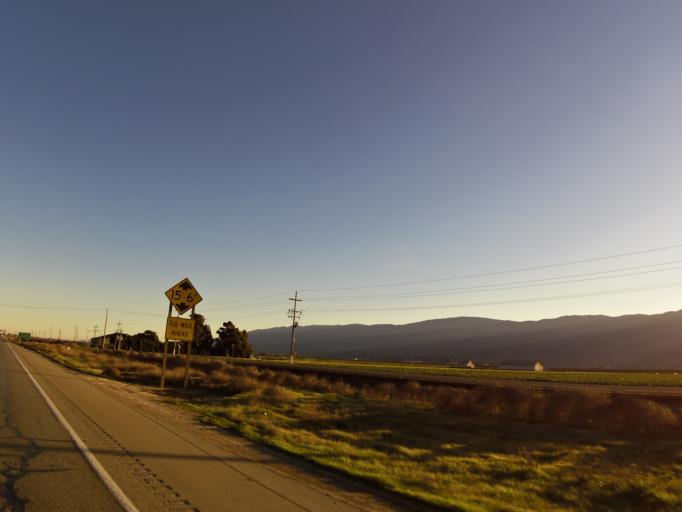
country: US
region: California
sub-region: Monterey County
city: Gonzales
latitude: 36.5311
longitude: -121.4752
